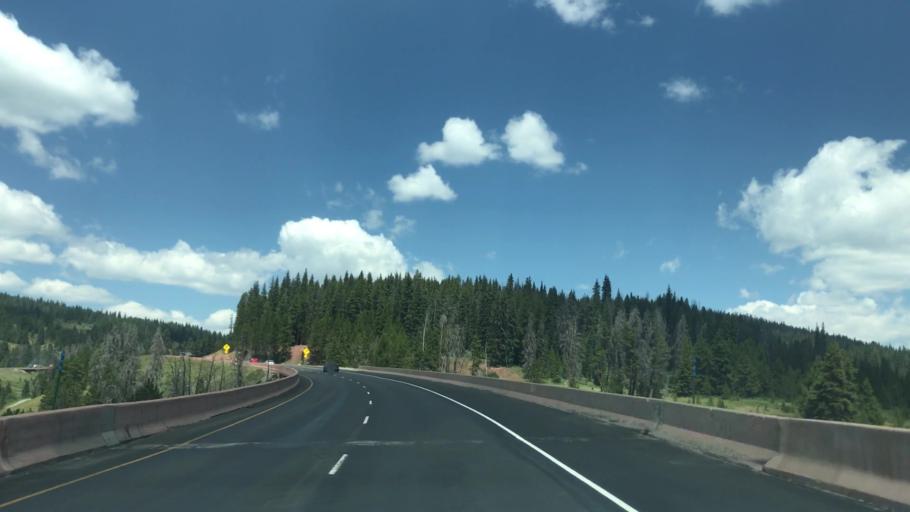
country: US
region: Colorado
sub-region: Summit County
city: Frisco
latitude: 39.5154
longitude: -106.2058
